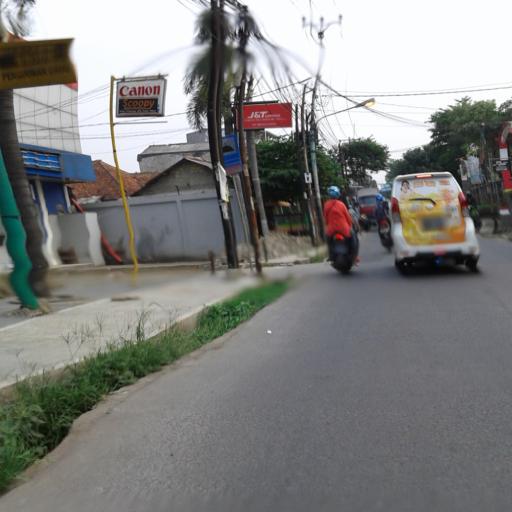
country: ID
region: West Java
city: Sawangan
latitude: -6.3818
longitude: 106.7690
